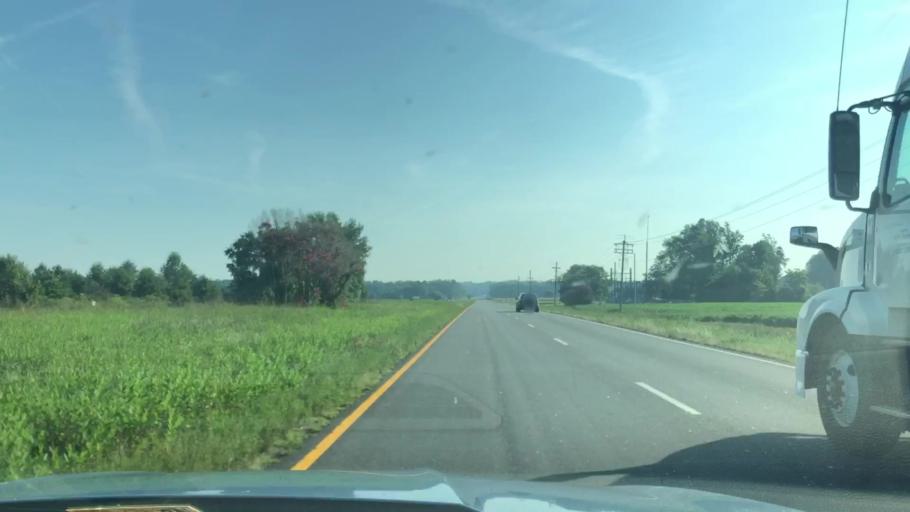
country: US
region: Virginia
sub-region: Essex County
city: Tappahannock
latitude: 37.9530
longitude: -76.8206
